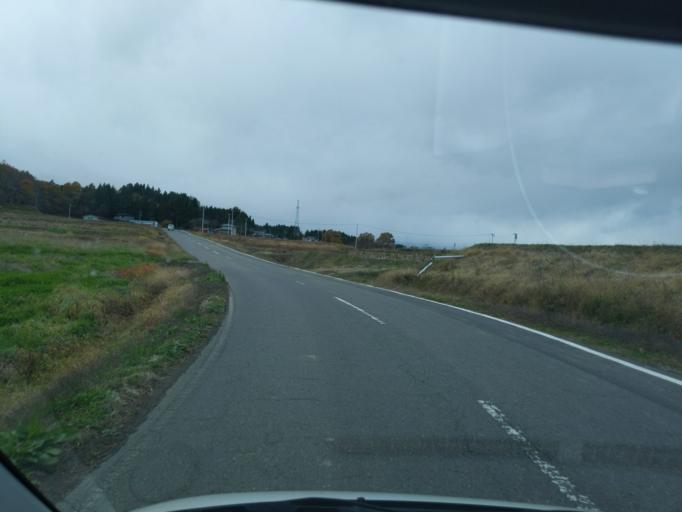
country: JP
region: Iwate
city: Mizusawa
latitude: 39.0471
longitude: 141.0749
